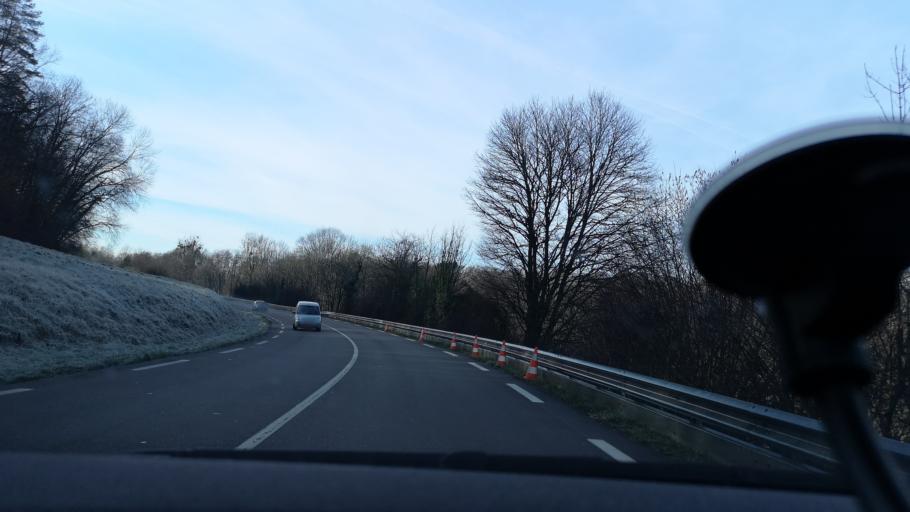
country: FR
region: Franche-Comte
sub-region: Departement du Doubs
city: Novillars
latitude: 47.3039
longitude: 6.1689
